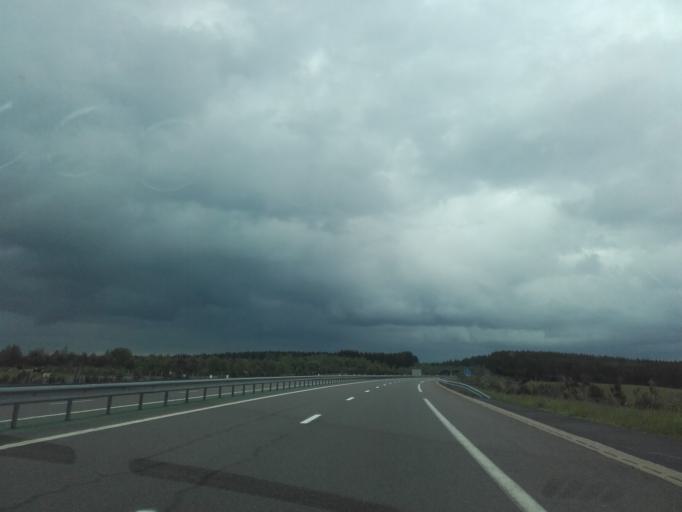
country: FR
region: Auvergne
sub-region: Departement du Puy-de-Dome
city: Gelles
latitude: 45.6986
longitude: 2.6946
